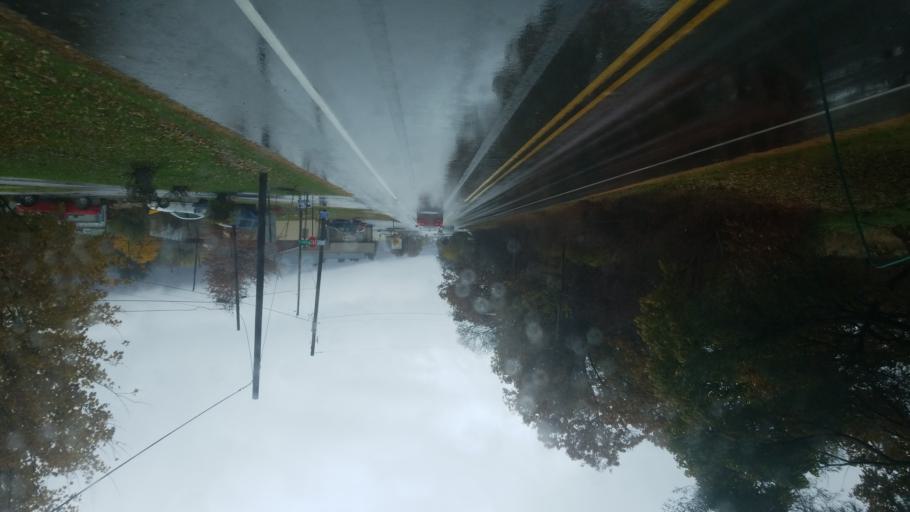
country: US
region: Pennsylvania
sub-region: Clinton County
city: Mill Hall
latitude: 41.1125
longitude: -77.4944
